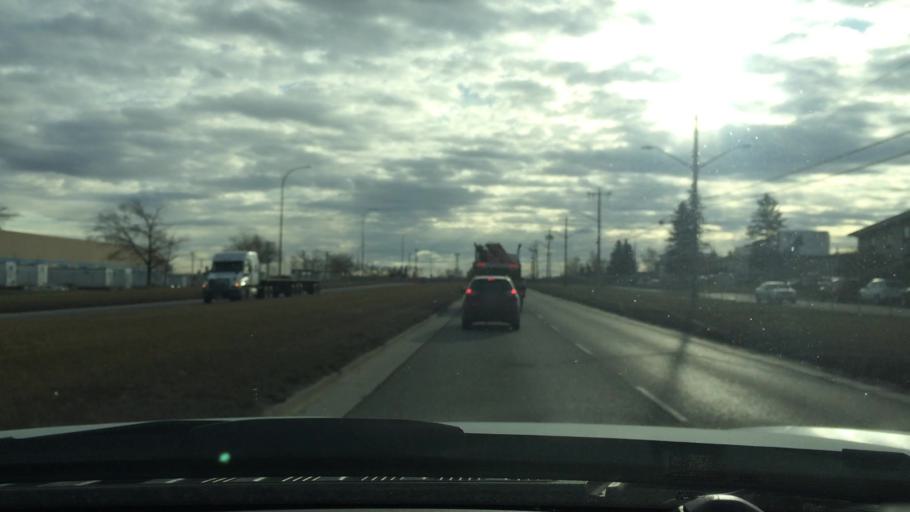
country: CA
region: Alberta
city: Calgary
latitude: 51.0033
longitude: -113.9921
